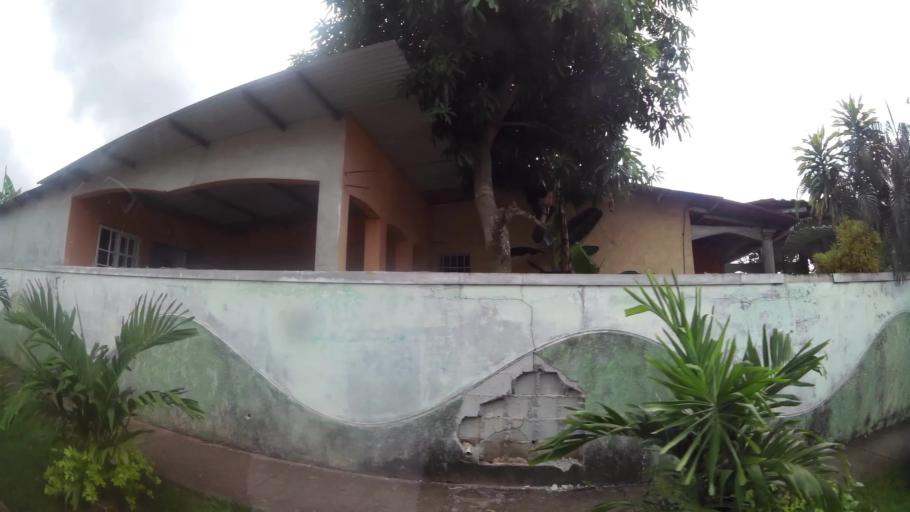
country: PA
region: Panama
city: Nuevo Arraijan
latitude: 8.9333
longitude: -79.7283
